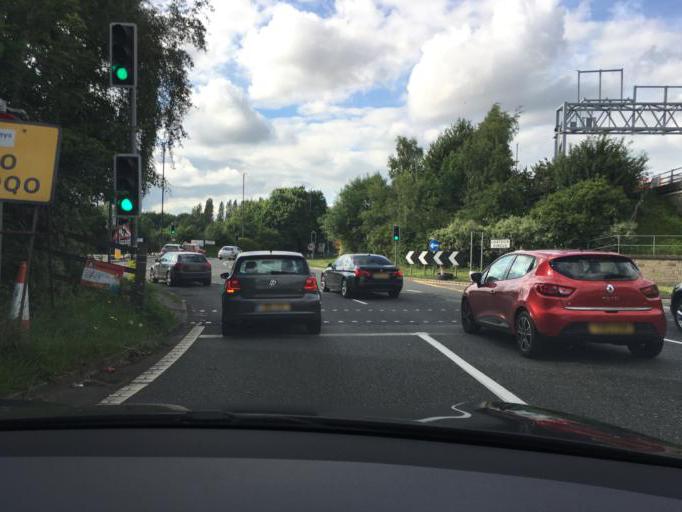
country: GB
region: England
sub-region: Trafford
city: Urmston
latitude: 53.4574
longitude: -2.3393
